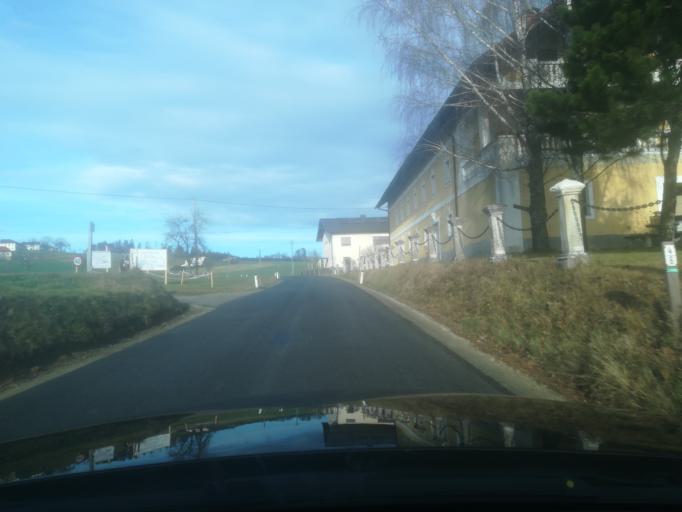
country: AT
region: Upper Austria
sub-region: Politischer Bezirk Perg
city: Perg
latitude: 48.3412
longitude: 14.6213
